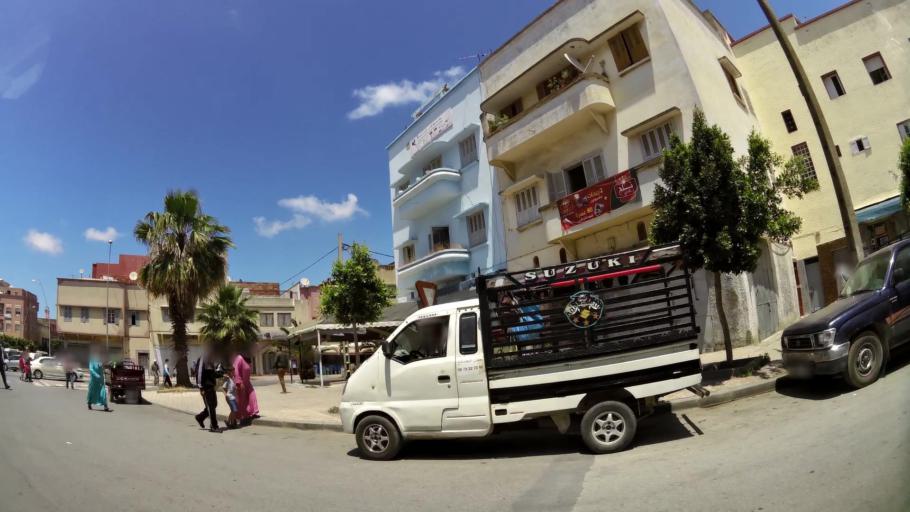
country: MA
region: Gharb-Chrarda-Beni Hssen
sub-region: Kenitra Province
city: Kenitra
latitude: 34.2598
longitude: -6.5599
